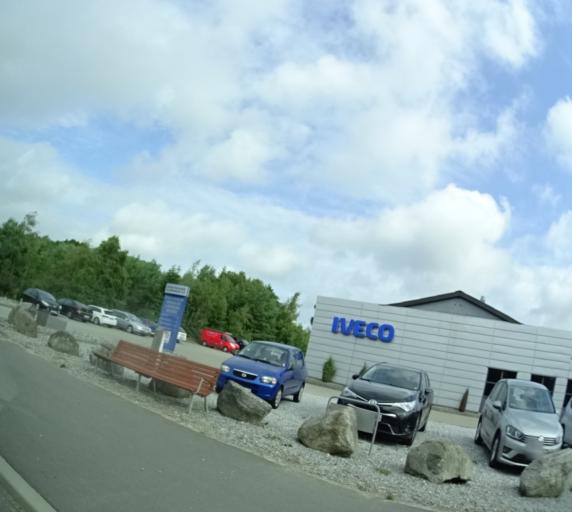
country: DK
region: Central Jutland
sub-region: Syddjurs Kommune
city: Ryomgard
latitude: 56.3832
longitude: 10.4850
